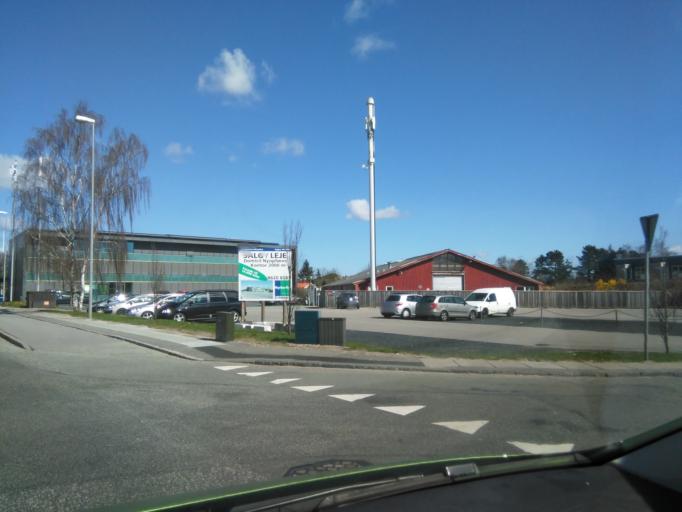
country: DK
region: Central Jutland
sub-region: Arhus Kommune
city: Lystrup
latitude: 56.2056
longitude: 10.2362
